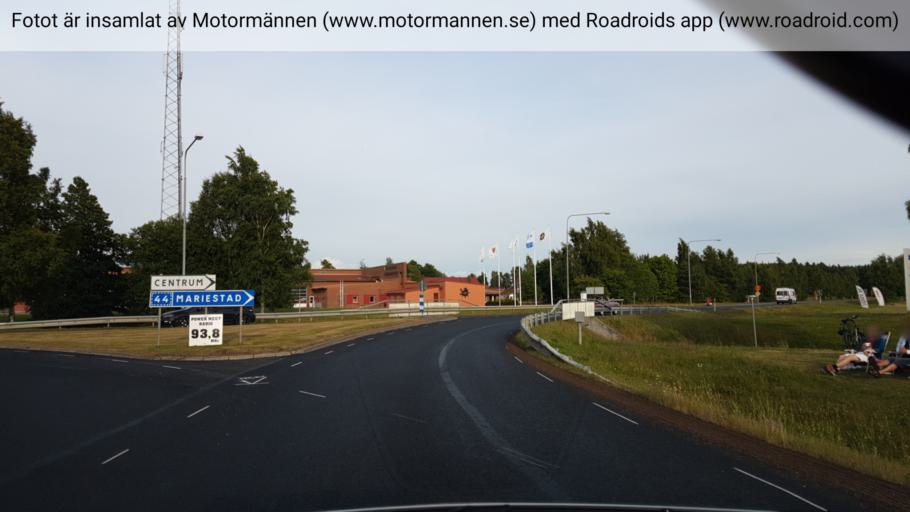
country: SE
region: Vaestra Goetaland
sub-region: Lidkopings Kommun
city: Lidkoping
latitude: 58.5027
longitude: 13.1254
